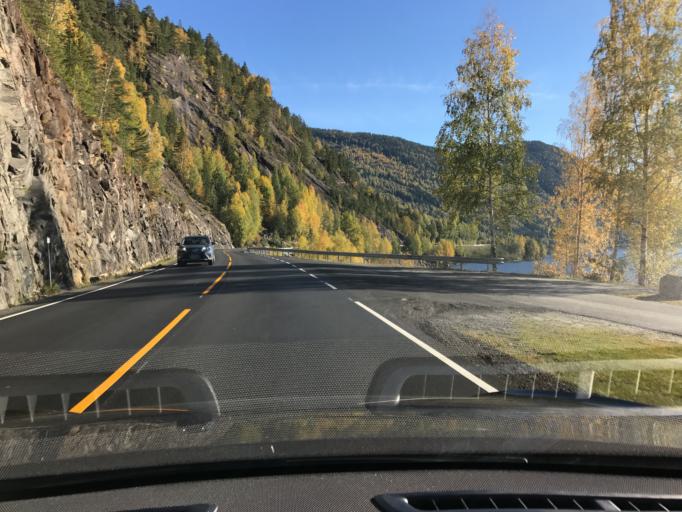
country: NO
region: Buskerud
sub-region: Krodsherad
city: Noresund
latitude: 60.3299
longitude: 9.6538
